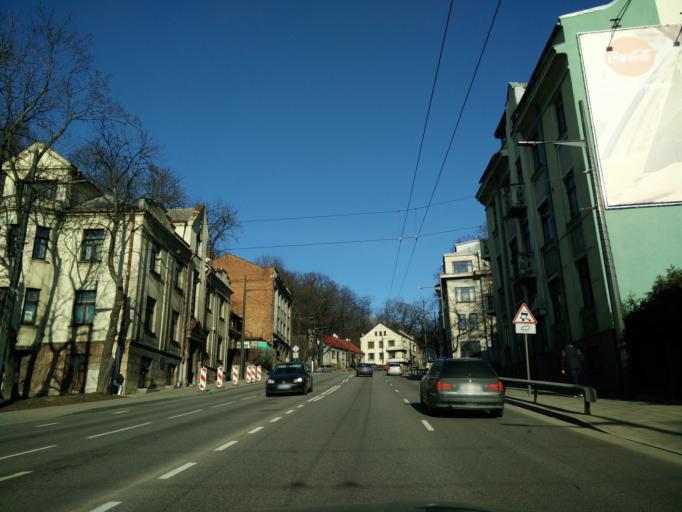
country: LT
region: Kauno apskritis
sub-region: Kaunas
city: Kaunas
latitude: 54.8977
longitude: 23.9263
